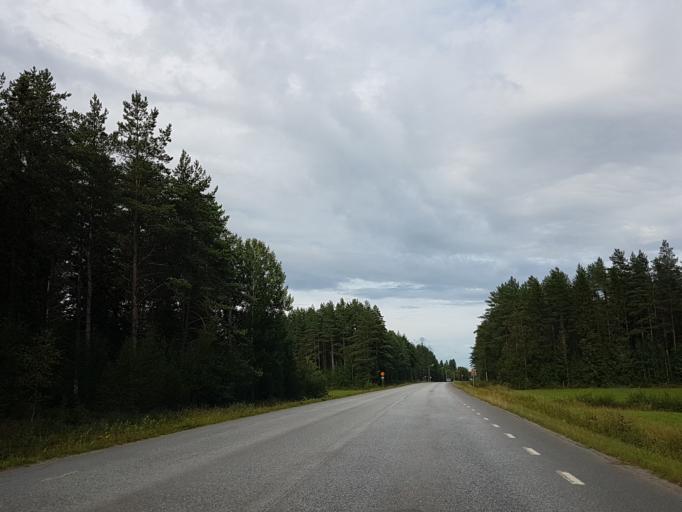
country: SE
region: Vaesterbotten
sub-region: Umea Kommun
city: Taftea
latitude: 63.8326
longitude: 20.4670
